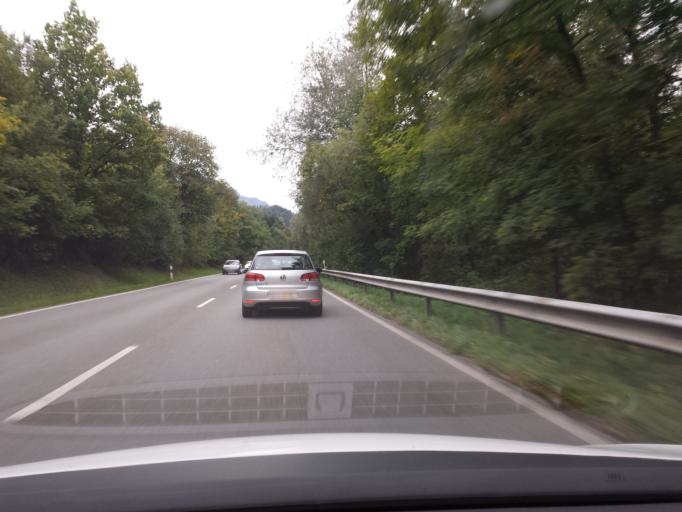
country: DE
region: Bavaria
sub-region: Upper Bavaria
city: Piding
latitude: 47.7486
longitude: 12.9126
